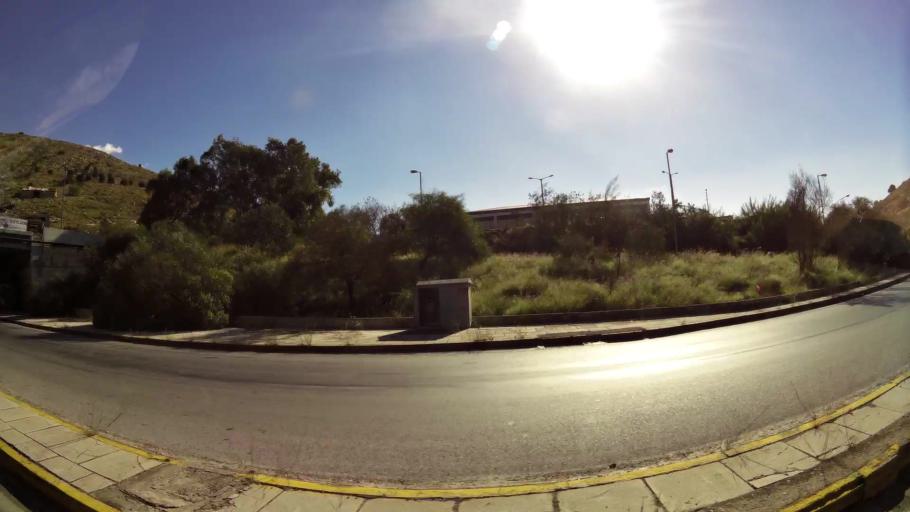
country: GR
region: Attica
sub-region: Nomos Piraios
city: Keratsini
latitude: 37.9690
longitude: 23.6055
